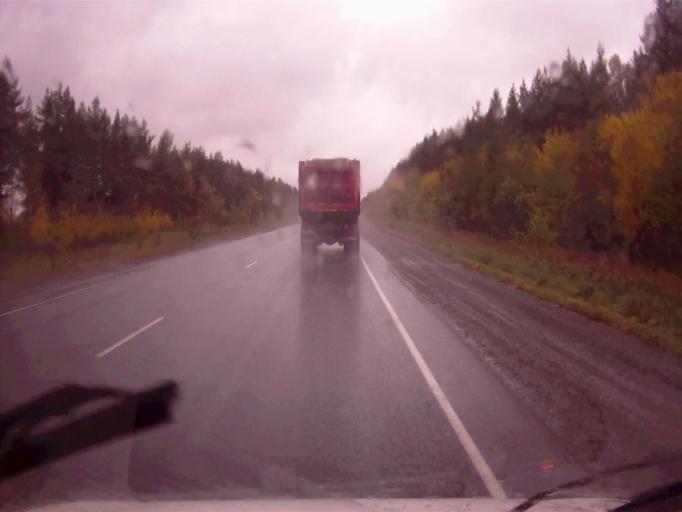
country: RU
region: Chelyabinsk
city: Roshchino
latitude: 55.3579
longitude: 61.2350
